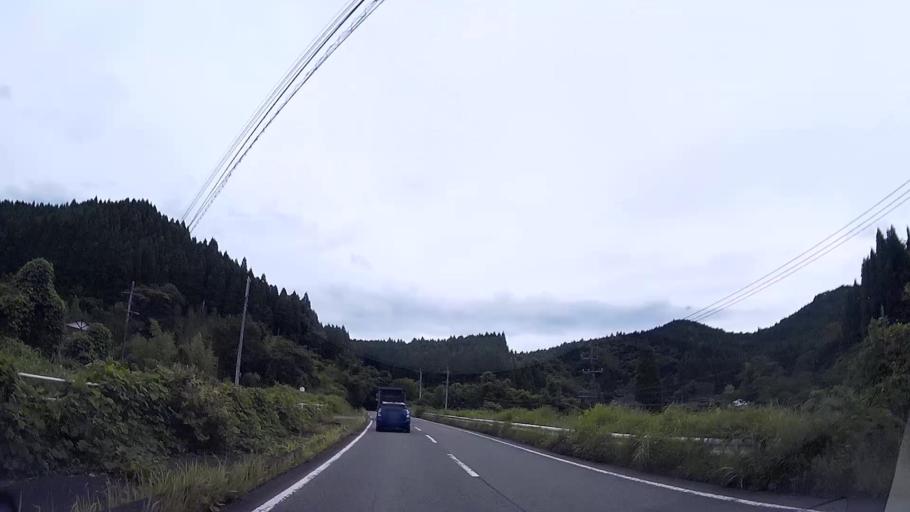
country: JP
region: Kumamoto
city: Aso
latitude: 33.1225
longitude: 131.0126
